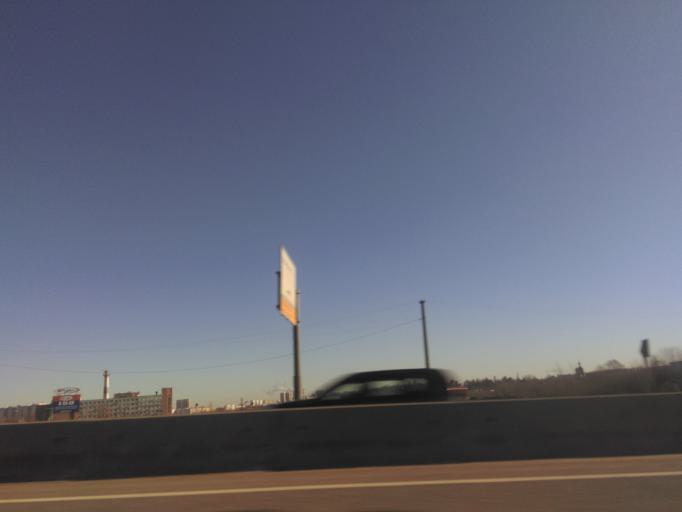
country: RU
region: Moskovskaya
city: Zarech'ye
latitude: 55.7007
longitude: 37.4005
